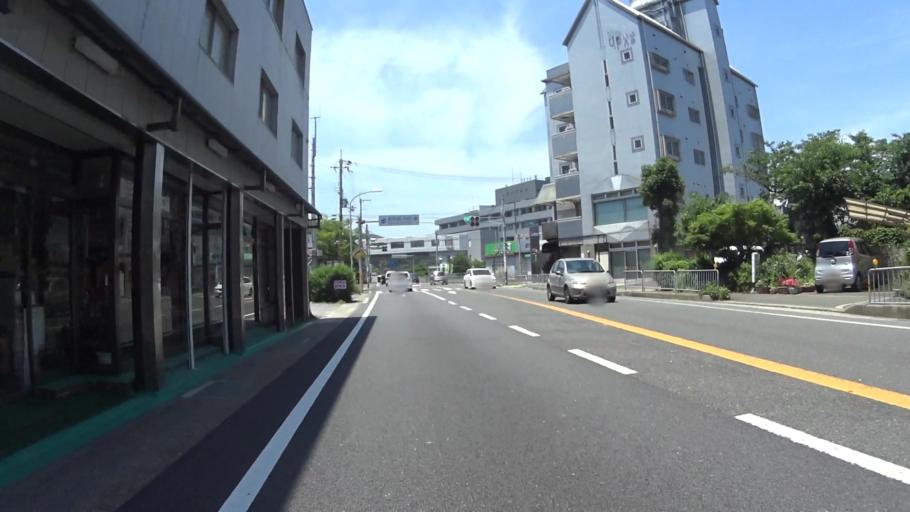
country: JP
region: Kyoto
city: Kameoka
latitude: 35.0700
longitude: 135.5318
